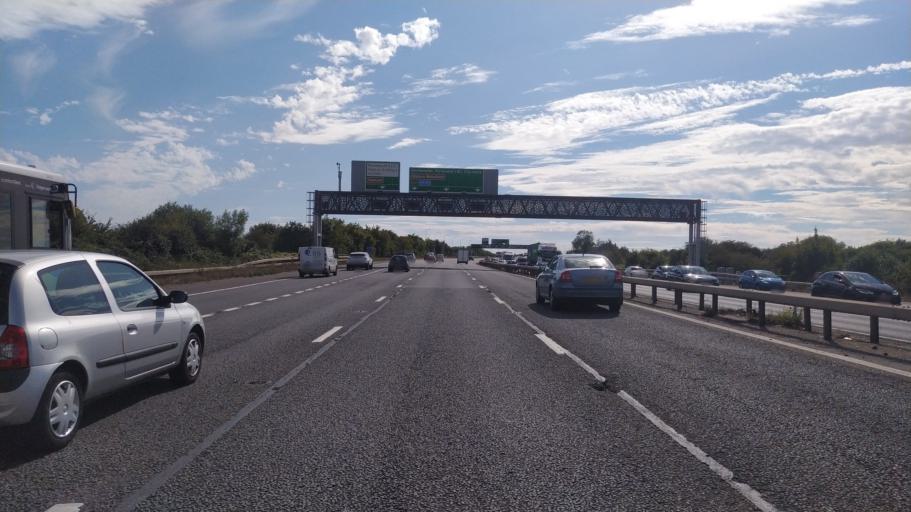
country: GB
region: England
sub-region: Portsmouth
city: Cosham
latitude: 50.8383
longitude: -1.0305
